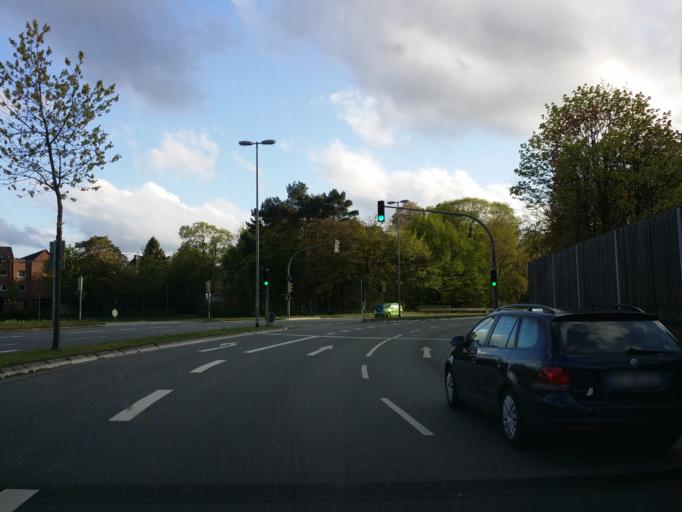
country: DE
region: Schleswig-Holstein
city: Rendsburg
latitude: 54.2946
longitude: 9.6629
